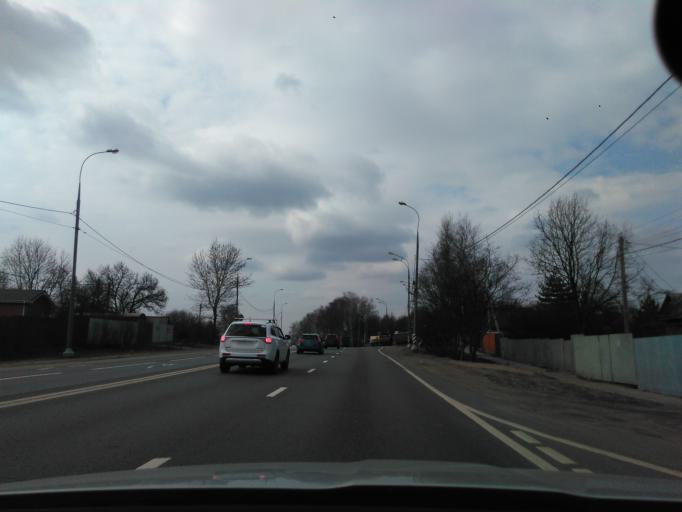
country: RU
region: Moskovskaya
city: Sheremet'yevskiy
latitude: 56.0064
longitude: 37.5420
